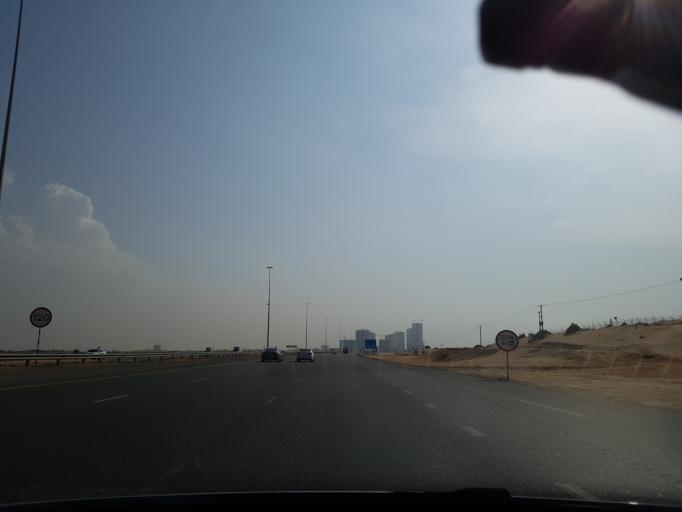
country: AE
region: Umm al Qaywayn
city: Umm al Qaywayn
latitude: 25.4160
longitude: 55.5881
